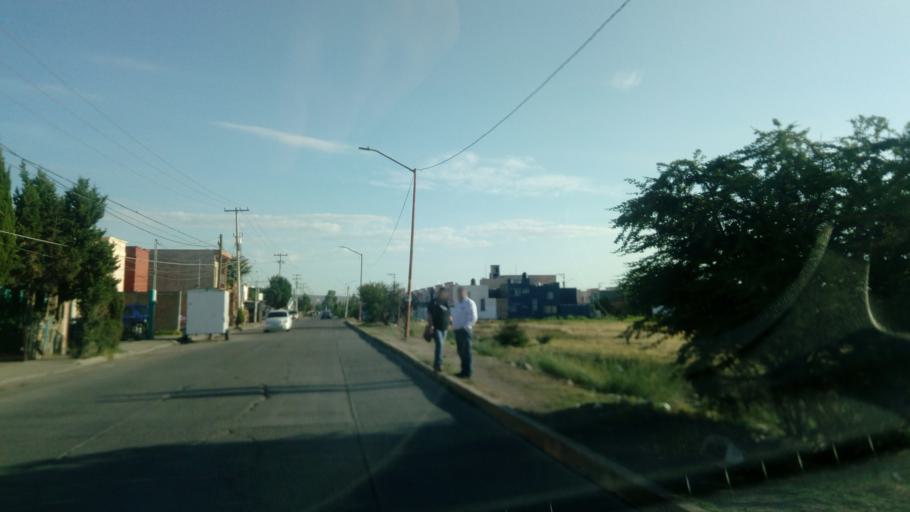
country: MX
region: Durango
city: Victoria de Durango
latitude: 24.0671
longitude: -104.5863
